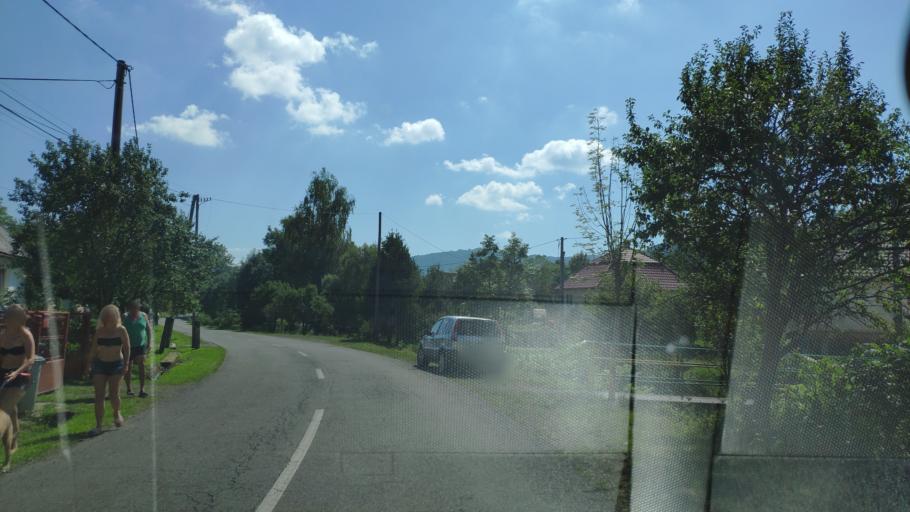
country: PL
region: Subcarpathian Voivodeship
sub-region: Powiat leski
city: Cisna
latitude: 49.0512
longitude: 22.3546
